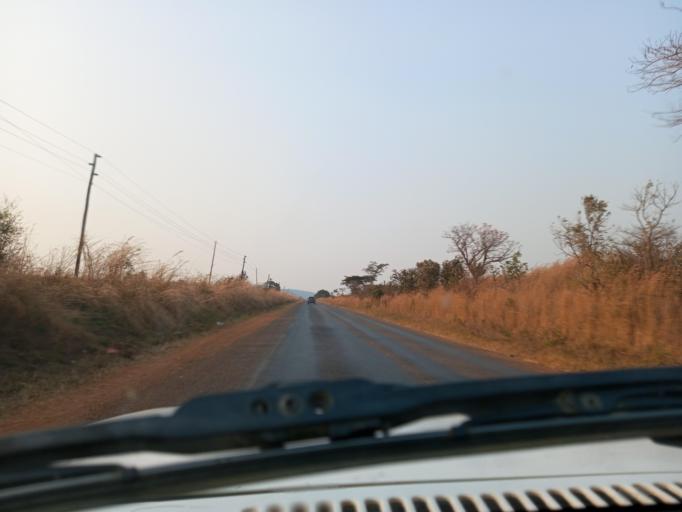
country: ZM
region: Northern
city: Mpika
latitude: -11.9039
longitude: 31.4139
